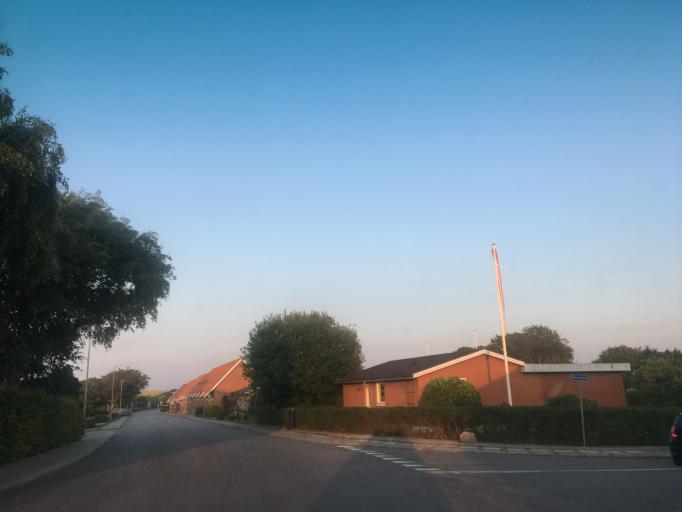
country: DK
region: North Denmark
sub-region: Thisted Kommune
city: Hurup
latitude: 56.7524
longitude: 8.4202
